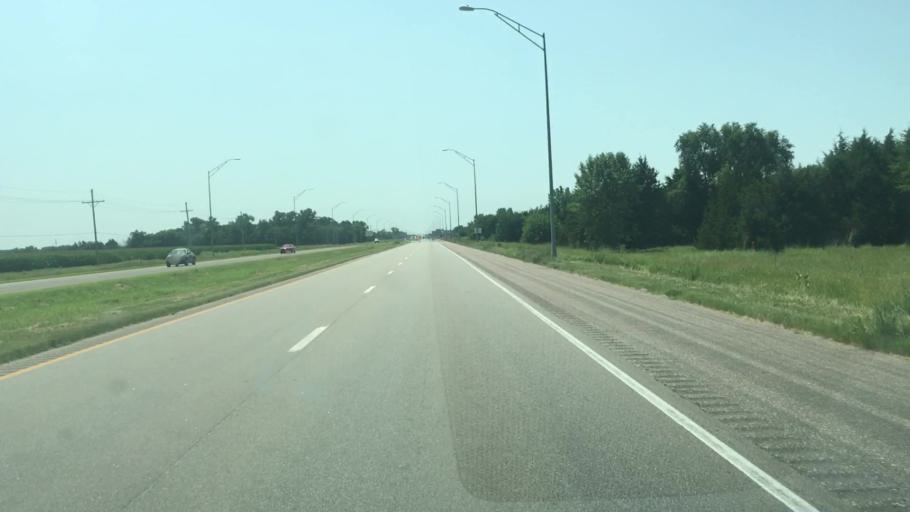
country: US
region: Nebraska
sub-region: Hall County
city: Grand Island
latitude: 40.8486
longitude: -98.3786
